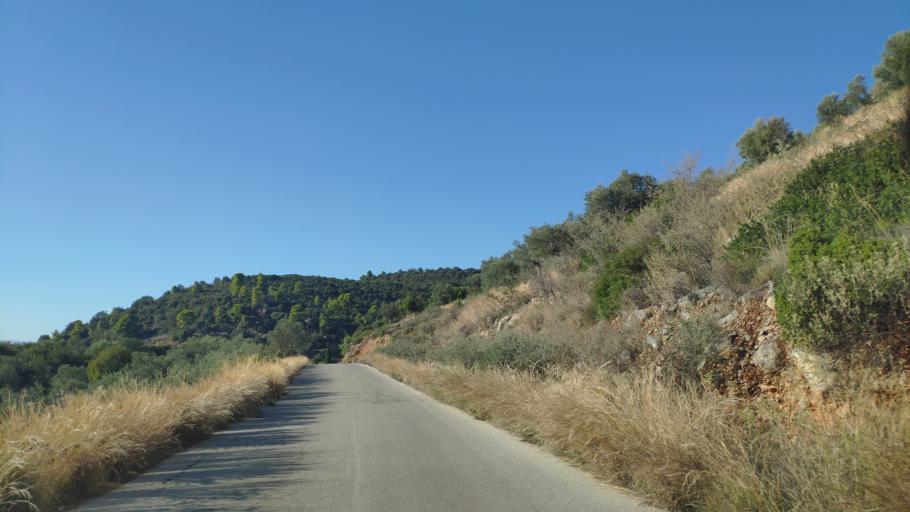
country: GR
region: Attica
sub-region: Nomos Piraios
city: Galatas
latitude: 37.5769
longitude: 23.3595
